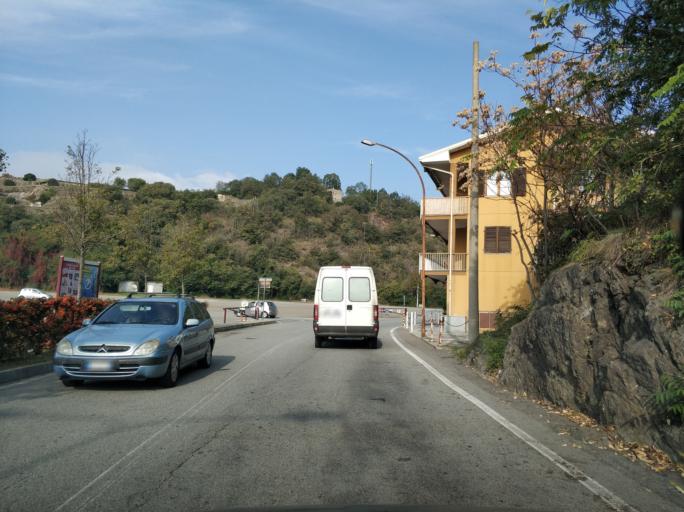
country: IT
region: Piedmont
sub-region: Provincia di Torino
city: Ivrea
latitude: 45.4714
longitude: 7.8806
